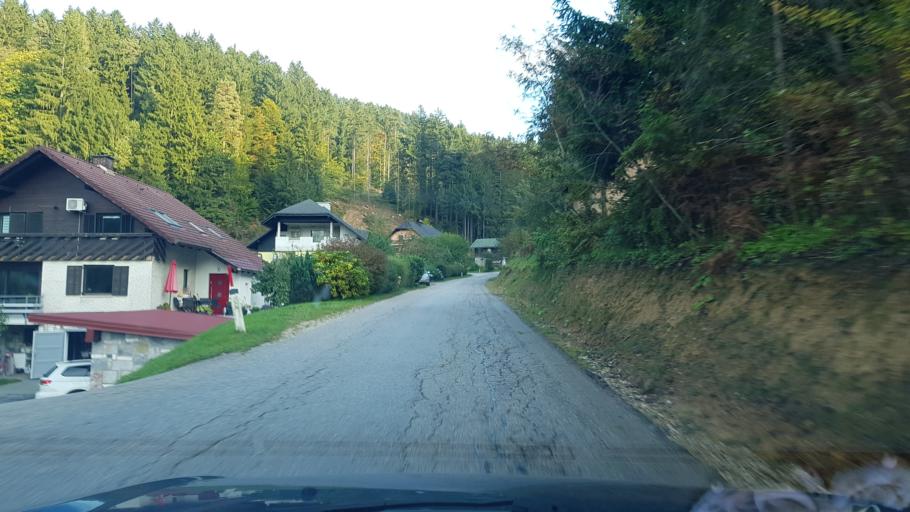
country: SI
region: Slovenj Gradec
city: Smartno pri Slovenj Gradcu
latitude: 46.5100
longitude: 15.1092
